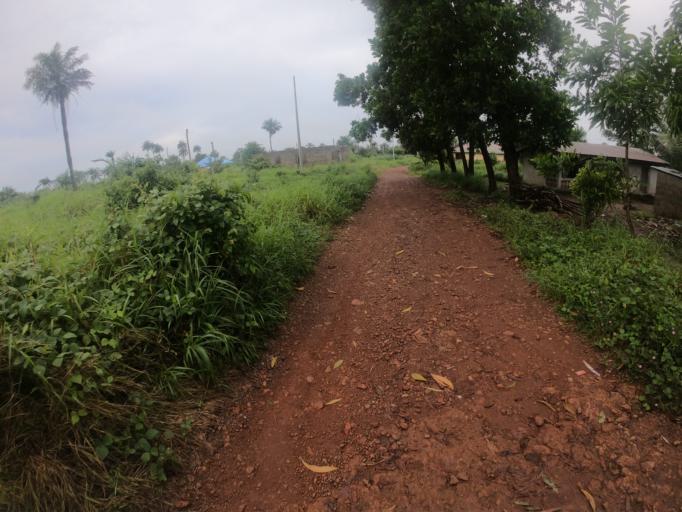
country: SL
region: Northern Province
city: Port Loko
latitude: 8.4960
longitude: -12.7509
